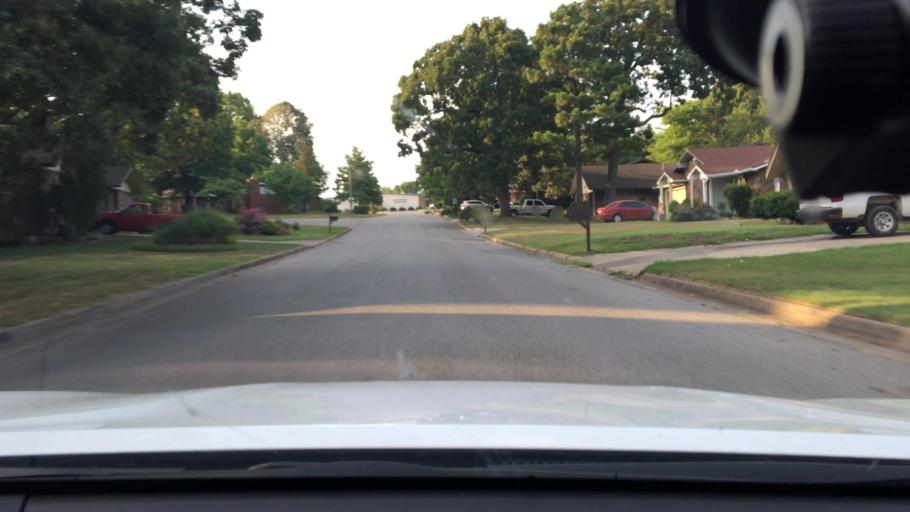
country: US
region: Arkansas
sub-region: Benton County
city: Rogers
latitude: 36.3397
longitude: -94.1620
